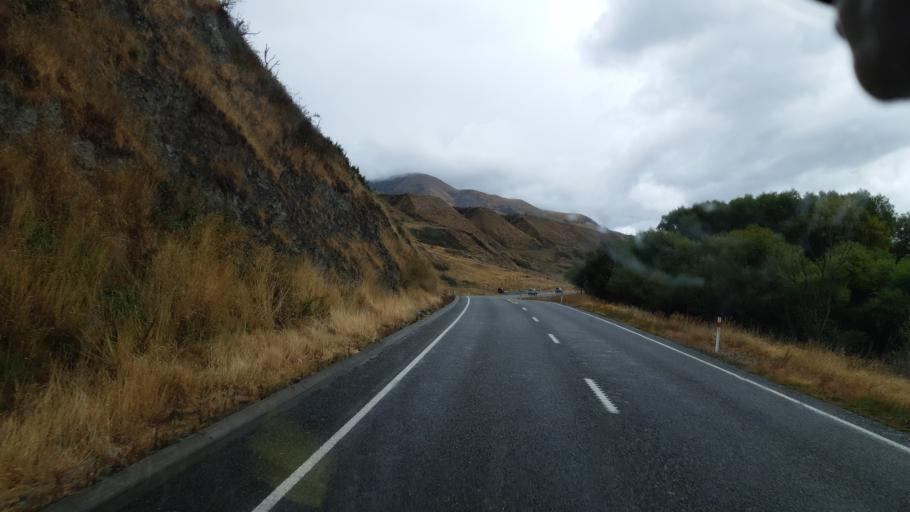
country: NZ
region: Canterbury
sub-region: Hurunui District
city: Amberley
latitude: -42.5783
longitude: 172.7515
